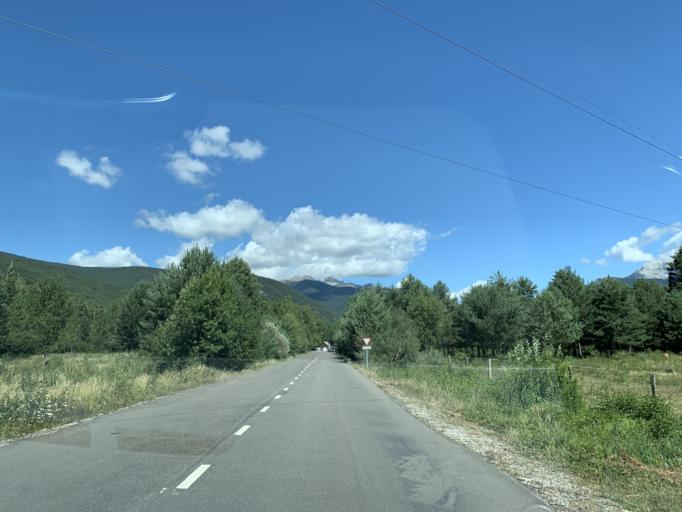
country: ES
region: Aragon
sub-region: Provincia de Huesca
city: Biescas
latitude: 42.5773
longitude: -0.3216
